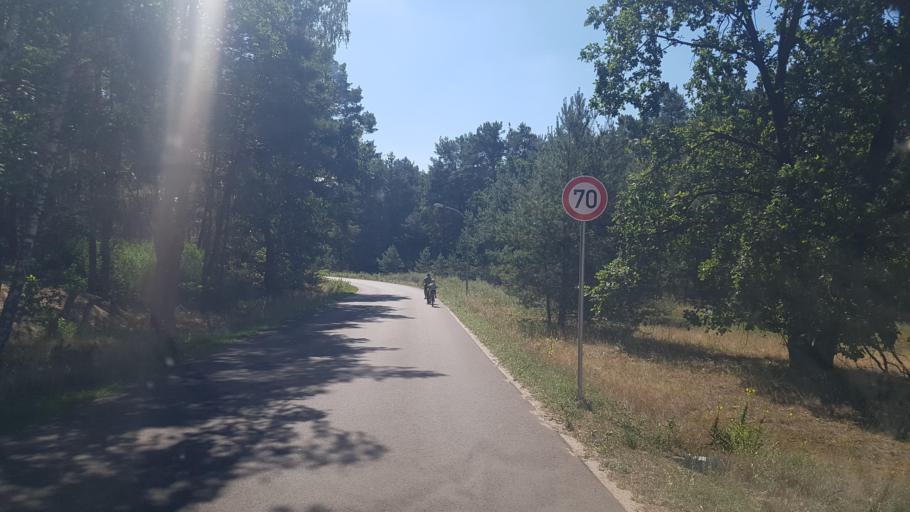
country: DE
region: Brandenburg
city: Golzow
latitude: 52.2930
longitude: 12.5877
